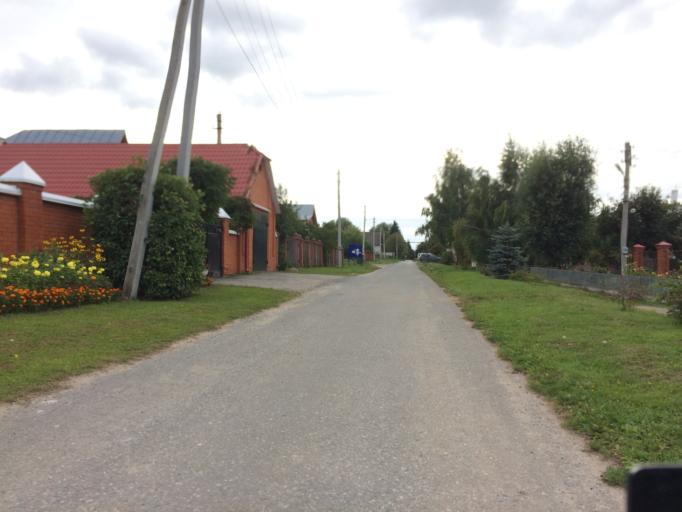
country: RU
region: Mariy-El
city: Yoshkar-Ola
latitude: 56.6657
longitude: 48.0001
